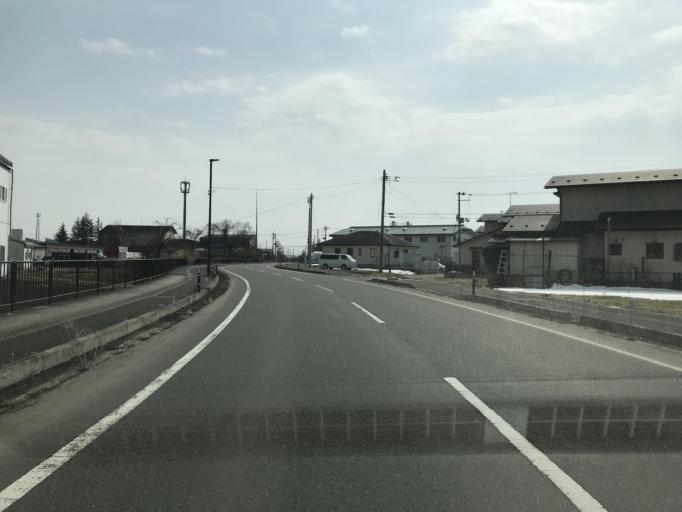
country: JP
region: Miyagi
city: Furukawa
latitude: 38.6542
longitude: 140.8722
